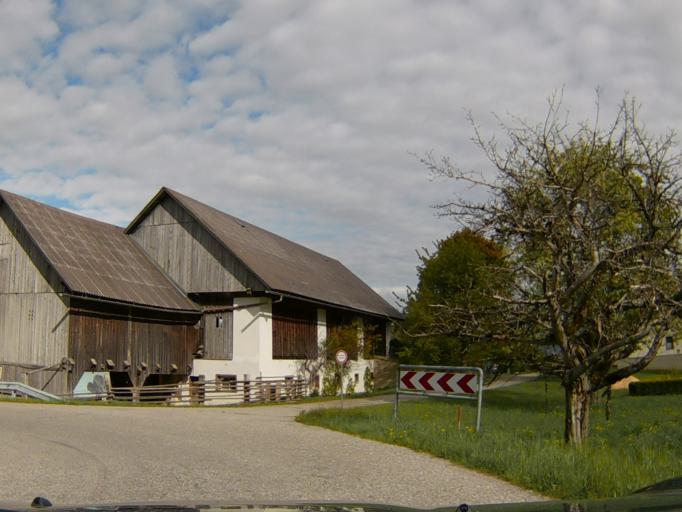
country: AT
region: Carinthia
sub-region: Politischer Bezirk Villach Land
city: Stockenboi
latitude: 46.7334
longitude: 13.5666
